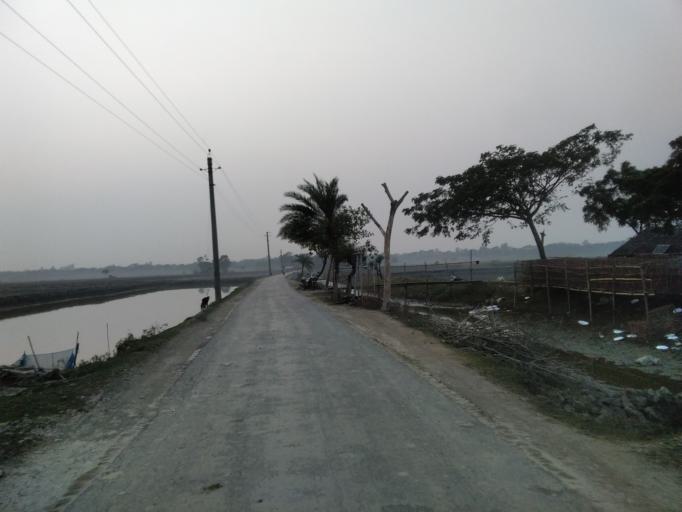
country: BD
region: Khulna
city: Satkhira
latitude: 22.6498
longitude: 89.0063
